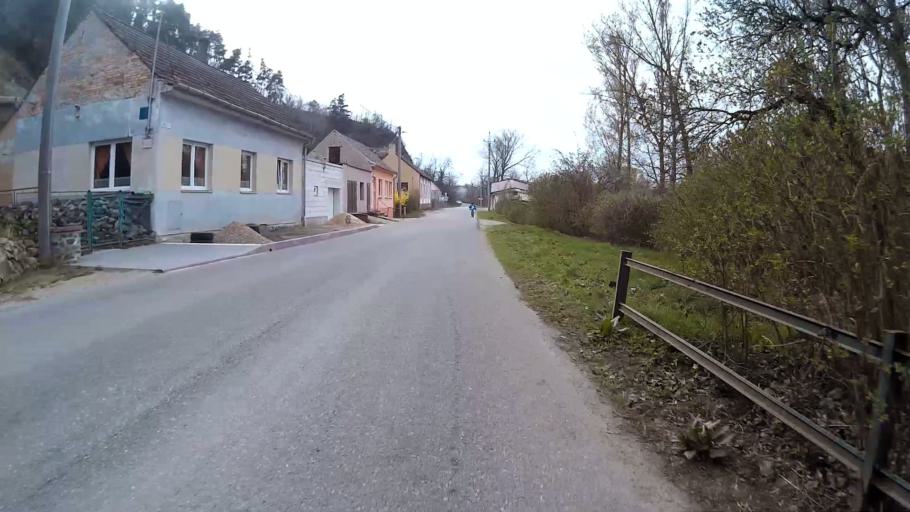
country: CZ
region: South Moravian
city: Dolni Kounice
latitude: 49.0703
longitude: 16.4538
